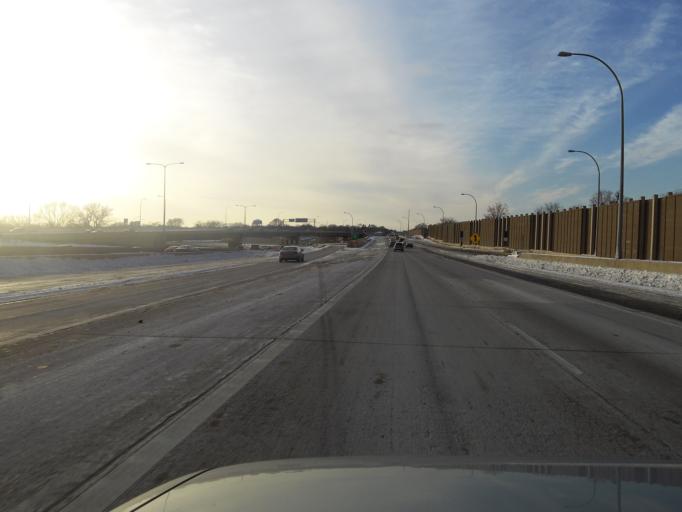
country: US
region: Minnesota
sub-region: Hennepin County
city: Richfield
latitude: 44.8905
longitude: -93.2907
